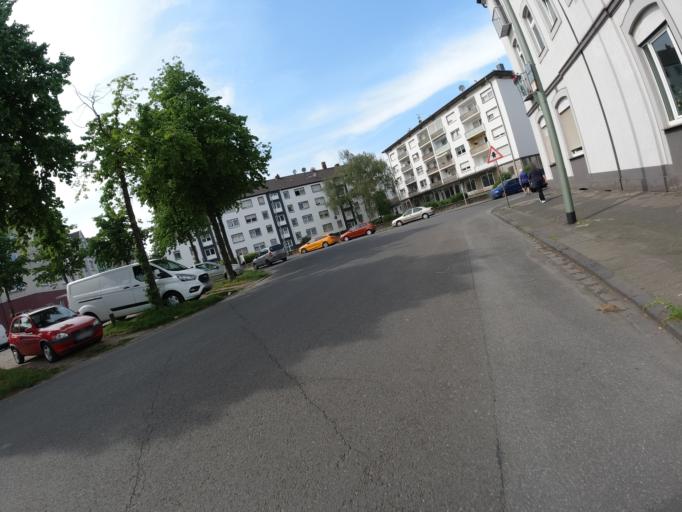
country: DE
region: North Rhine-Westphalia
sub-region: Regierungsbezirk Dusseldorf
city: Hochfeld
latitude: 51.3925
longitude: 6.7119
